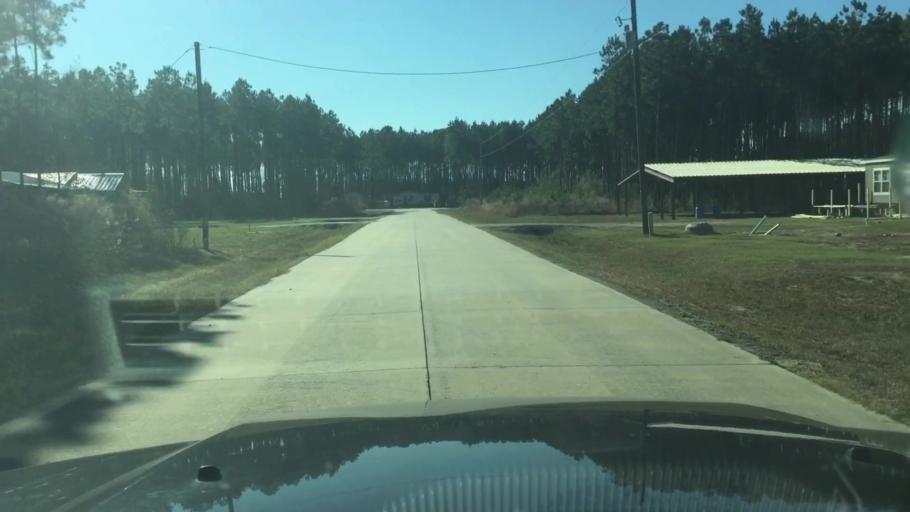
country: US
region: Texas
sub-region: Montgomery County
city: Roman Forest
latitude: 30.1734
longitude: -95.0852
